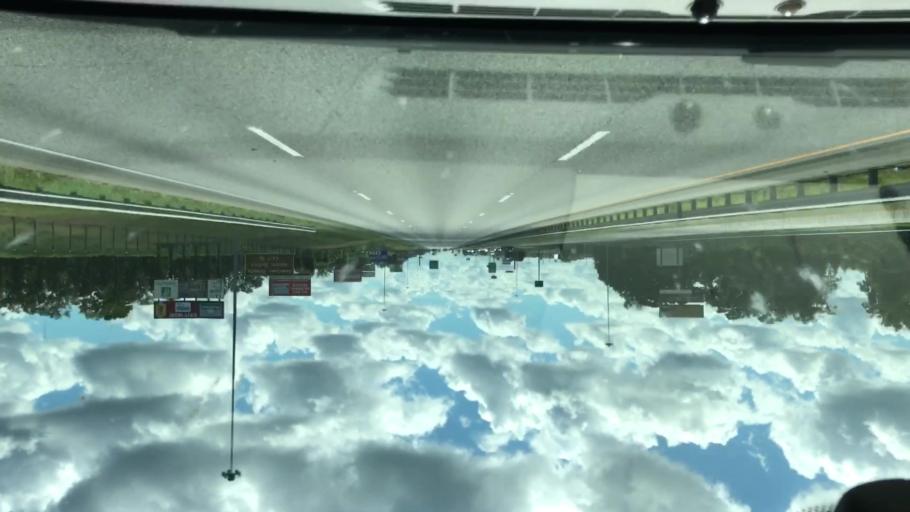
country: US
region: Georgia
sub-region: Lowndes County
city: Remerton
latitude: 30.8322
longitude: -83.3247
